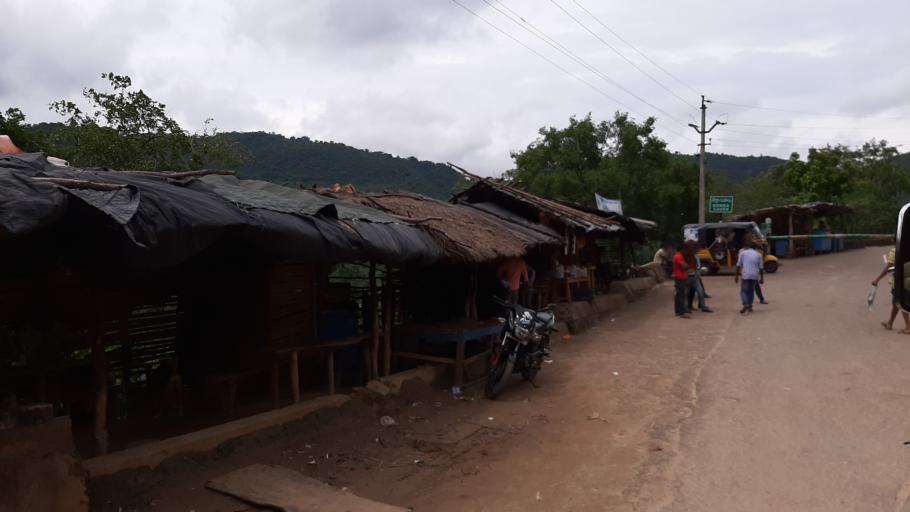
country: IN
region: Andhra Pradesh
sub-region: Vizianagaram District
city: Salur
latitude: 18.2789
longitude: 83.0379
